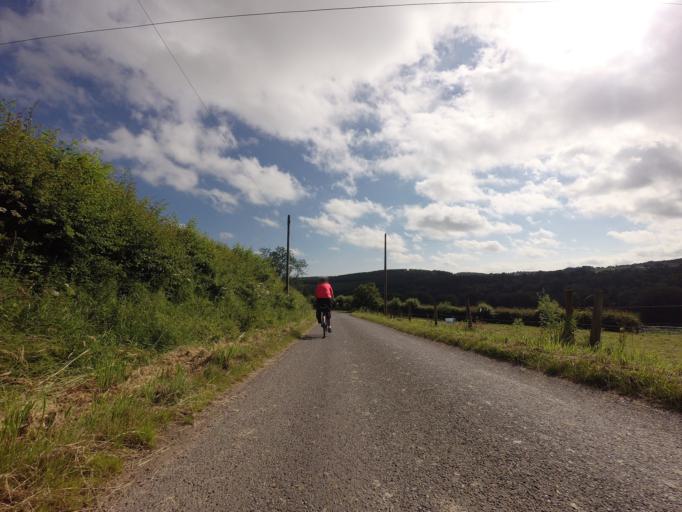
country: GB
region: Scotland
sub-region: Aberdeenshire
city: Turriff
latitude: 57.5827
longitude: -2.5067
